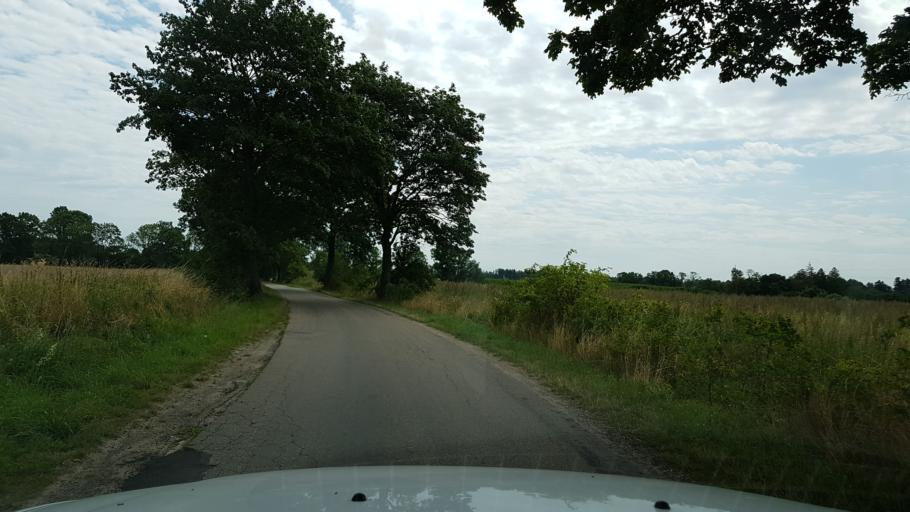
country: PL
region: West Pomeranian Voivodeship
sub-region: Powiat koszalinski
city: Mielno
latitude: 54.1682
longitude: 16.0560
